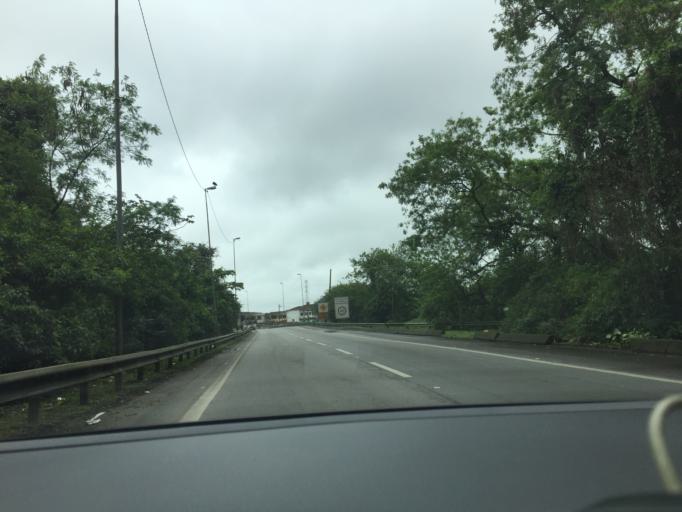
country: BR
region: Sao Paulo
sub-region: Guaruja
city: Guaruja
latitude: -23.9678
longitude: -46.2717
